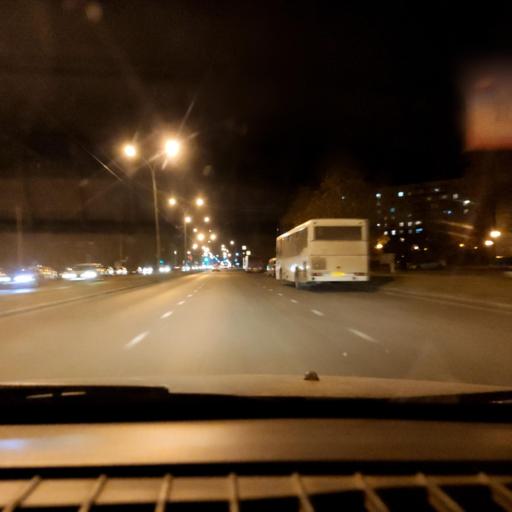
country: RU
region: Samara
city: Tol'yatti
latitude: 53.5383
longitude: 49.3149
